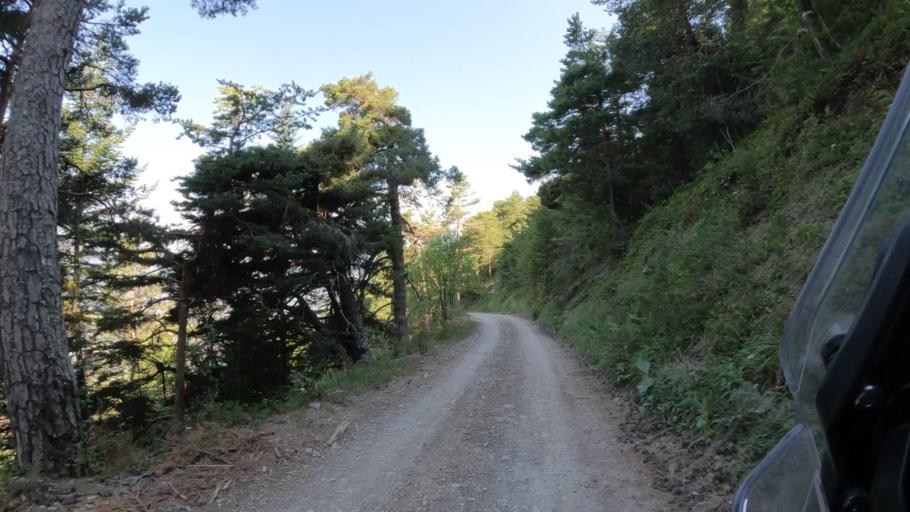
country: FR
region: Provence-Alpes-Cote d'Azur
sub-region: Departement des Hautes-Alpes
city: Embrun
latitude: 44.5969
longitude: 6.5646
